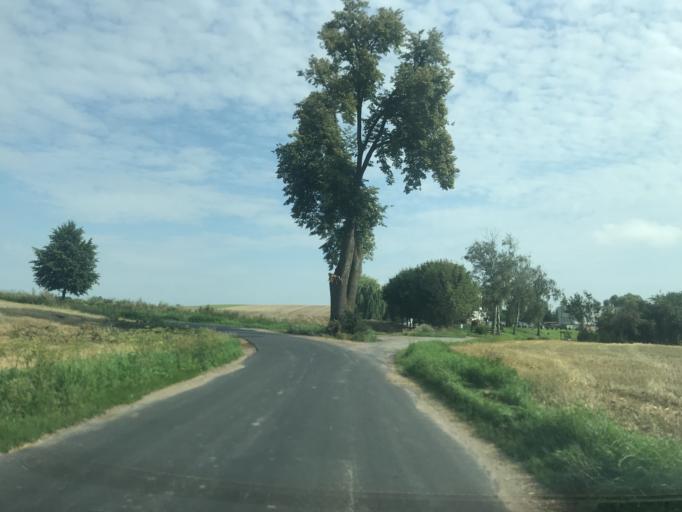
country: PL
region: Warmian-Masurian Voivodeship
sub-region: Powiat nowomiejski
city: Kurzetnik
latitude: 53.3649
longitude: 19.5903
